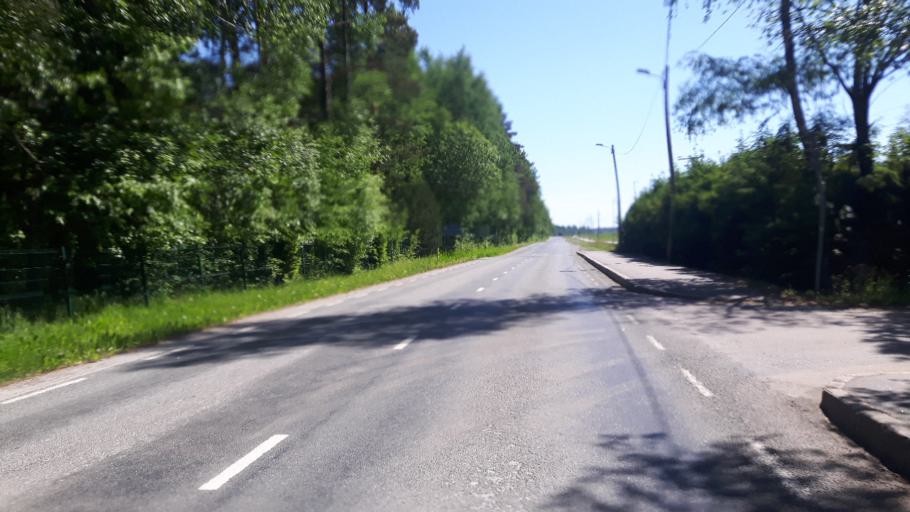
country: EE
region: Harju
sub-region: Saku vald
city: Saku
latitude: 59.2178
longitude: 24.6754
